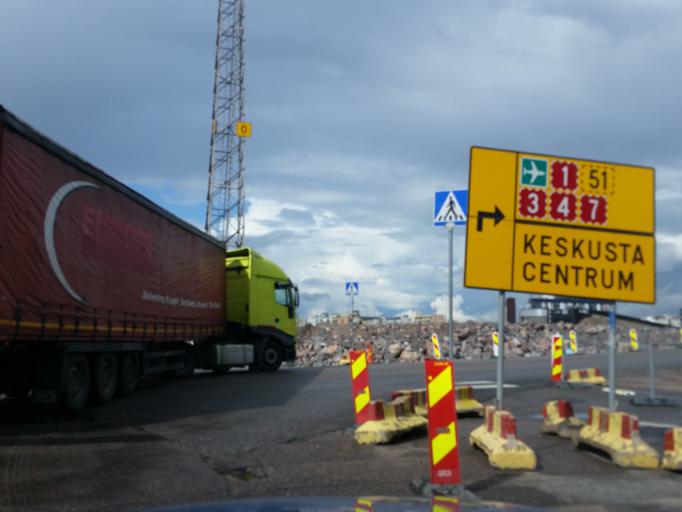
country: FI
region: Uusimaa
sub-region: Helsinki
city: Helsinki
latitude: 60.1543
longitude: 24.9144
